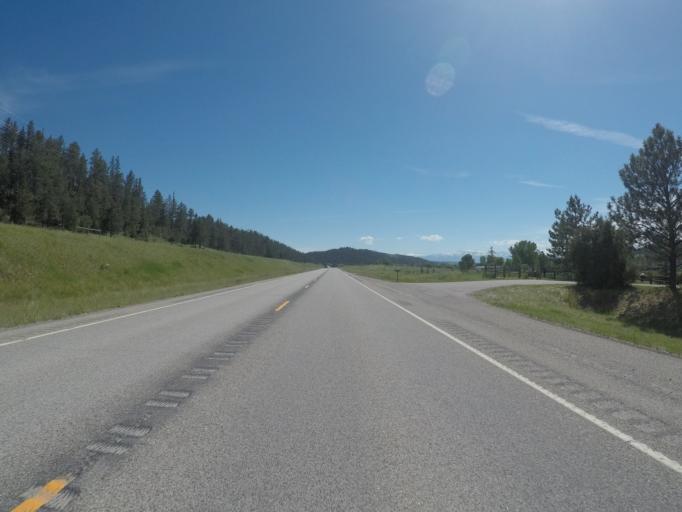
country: US
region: Montana
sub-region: Stillwater County
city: Columbus
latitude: 45.6052
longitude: -109.2875
